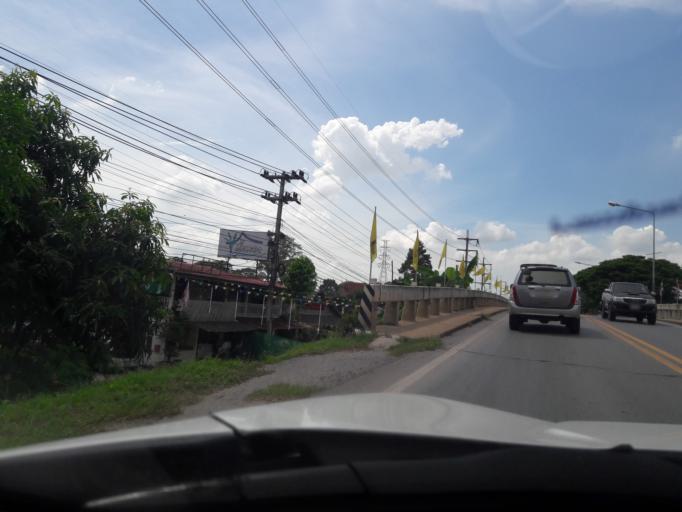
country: TH
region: Ang Thong
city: Ban Thai Tan
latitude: 14.5791
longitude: 100.5085
